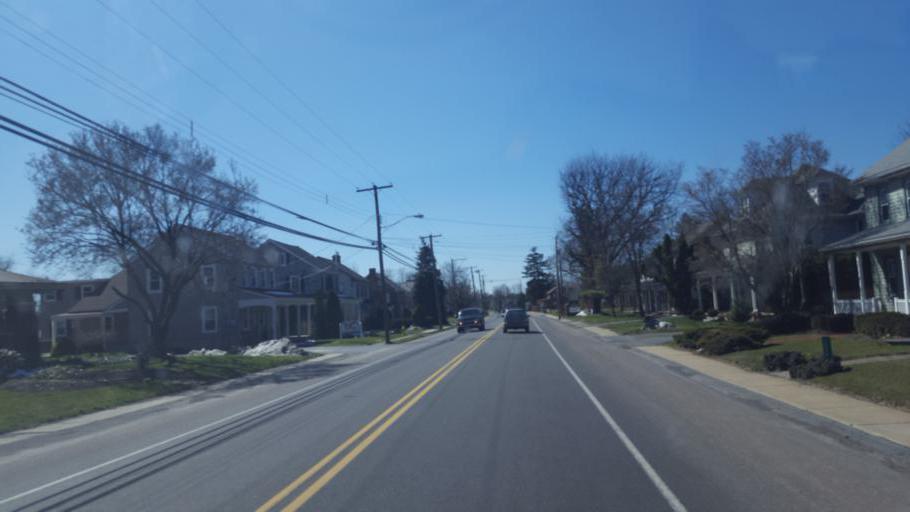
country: US
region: Pennsylvania
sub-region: Lancaster County
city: Brownstown
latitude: 40.0913
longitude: -76.1658
